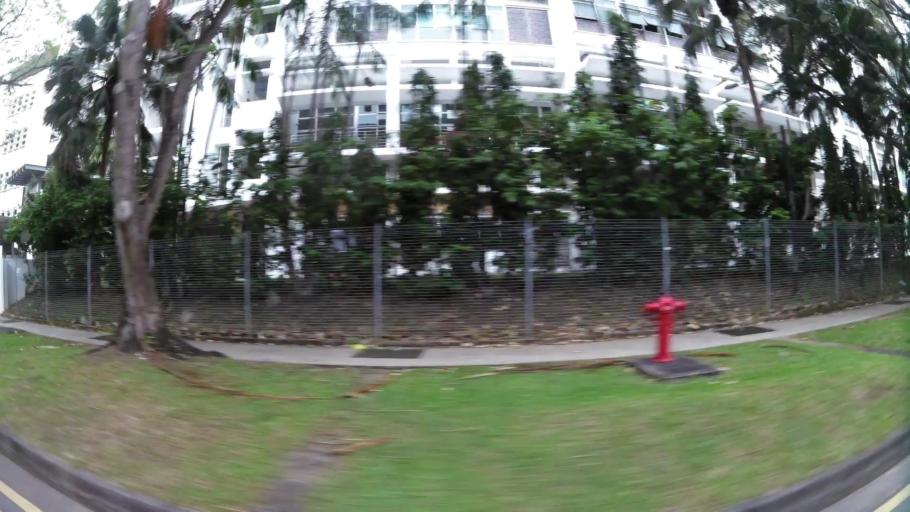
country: MY
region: Johor
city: Kampung Pasir Gudang Baru
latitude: 1.4381
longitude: 103.8405
